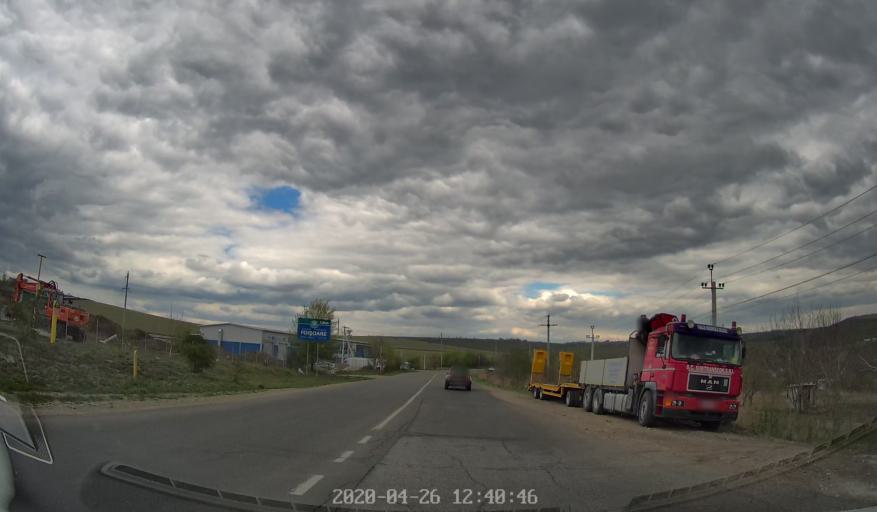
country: MD
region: Chisinau
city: Chisinau
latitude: 47.0439
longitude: 28.9076
